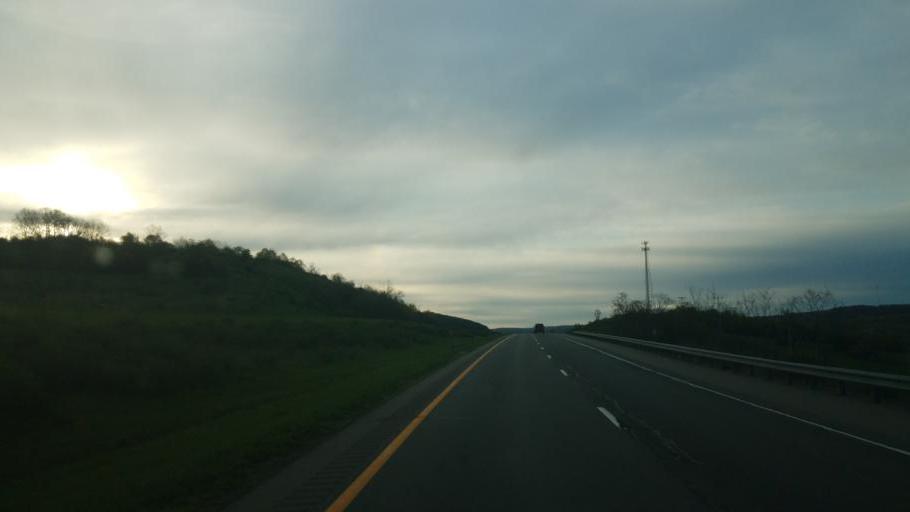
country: US
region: New York
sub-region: Allegany County
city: Friendship
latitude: 42.2112
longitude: -78.2038
